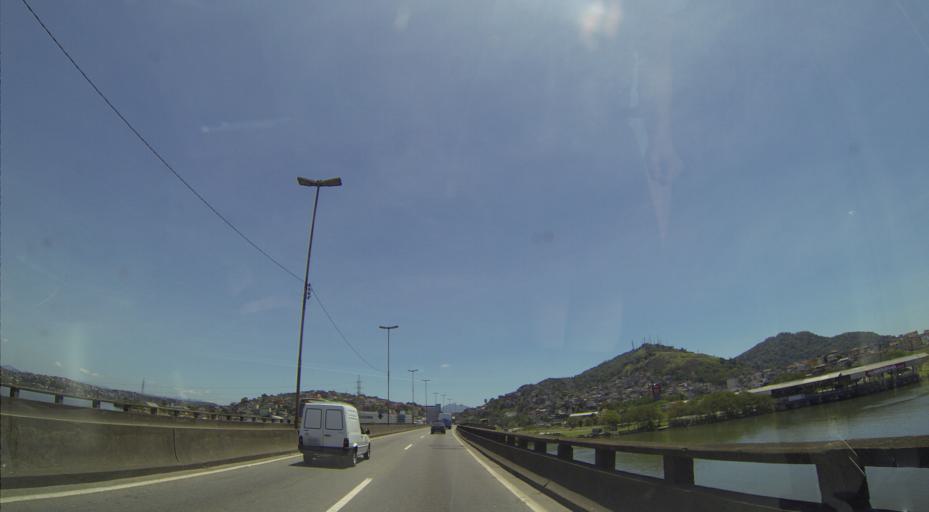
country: BR
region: Espirito Santo
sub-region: Vitoria
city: Vitoria
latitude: -20.3246
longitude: -40.3545
